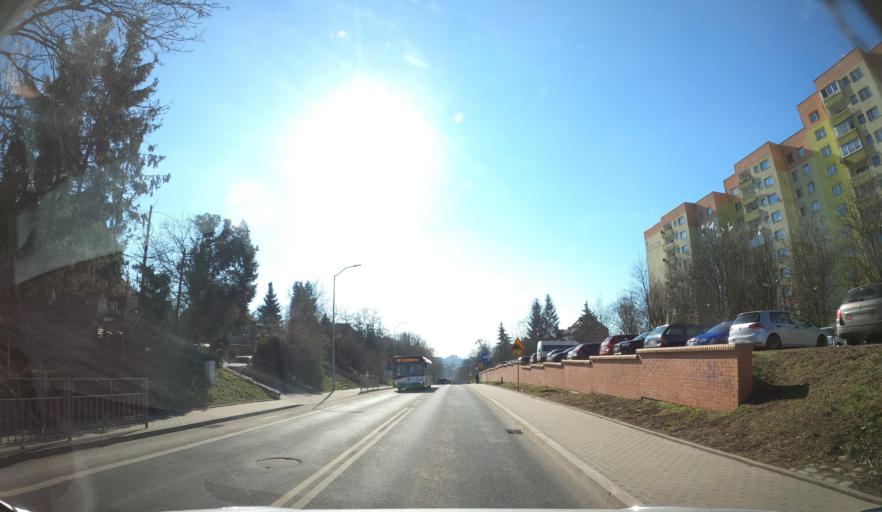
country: PL
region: West Pomeranian Voivodeship
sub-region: Szczecin
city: Szczecin
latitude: 53.4526
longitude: 14.5504
